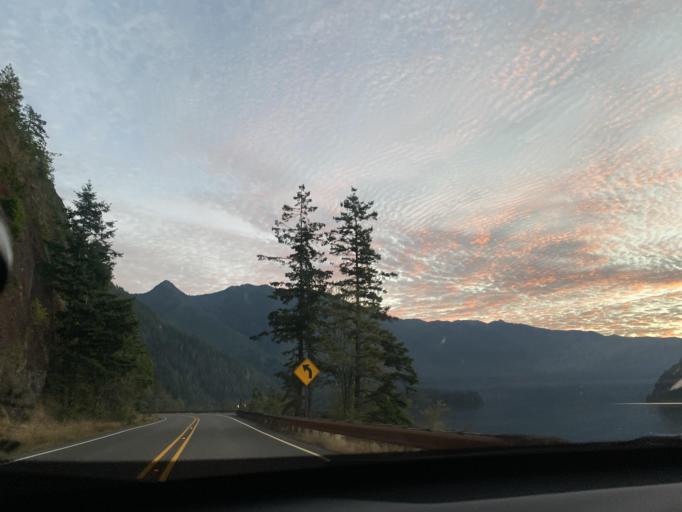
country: CA
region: British Columbia
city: Sooke
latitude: 48.0730
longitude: -123.7734
